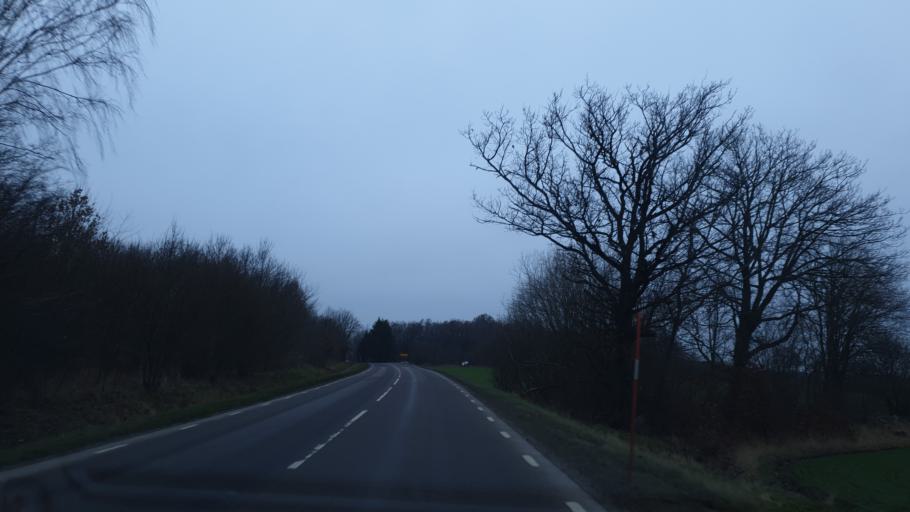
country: SE
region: Blekinge
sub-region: Karlskrona Kommun
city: Jaemjoe
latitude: 56.1571
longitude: 15.7644
